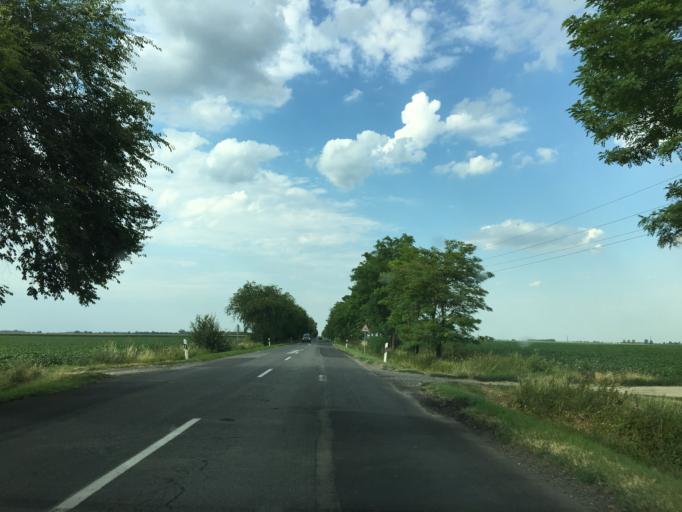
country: HU
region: Bacs-Kiskun
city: Dusnok
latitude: 46.4366
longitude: 18.9479
